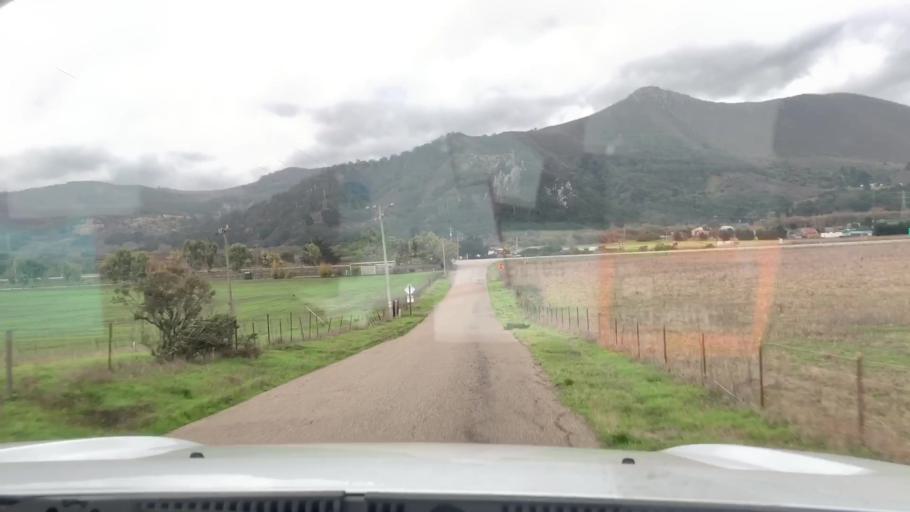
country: US
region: California
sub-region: San Luis Obispo County
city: Morro Bay
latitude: 35.3643
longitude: -120.8067
